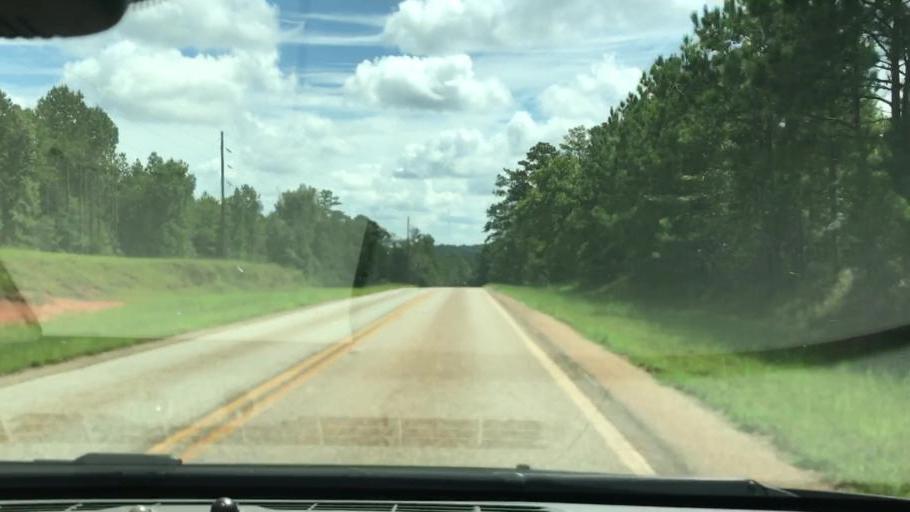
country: US
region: Georgia
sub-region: Stewart County
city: Lumpkin
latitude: 32.0616
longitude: -84.8274
